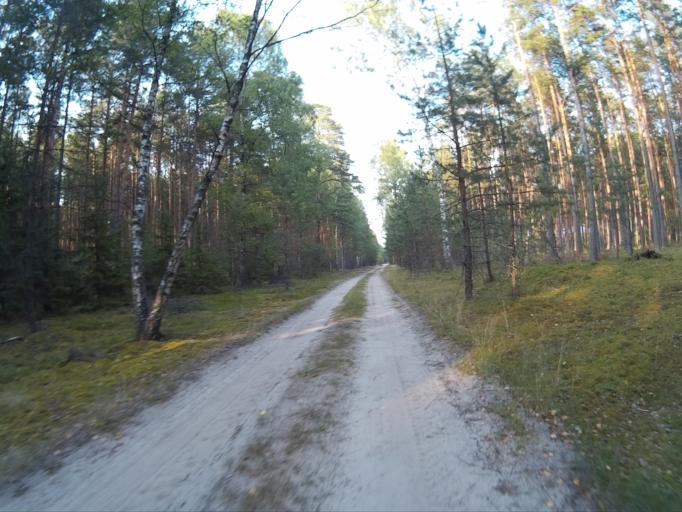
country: PL
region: Pomeranian Voivodeship
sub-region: Powiat chojnicki
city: Czersk
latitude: 53.6972
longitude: 17.9654
